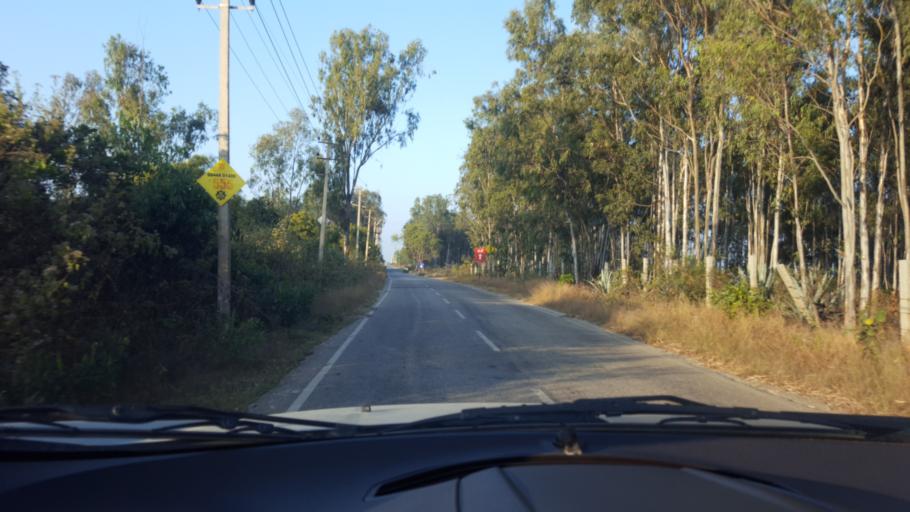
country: IN
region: Karnataka
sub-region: Bangalore Urban
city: Yelahanka
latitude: 13.1865
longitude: 77.5999
